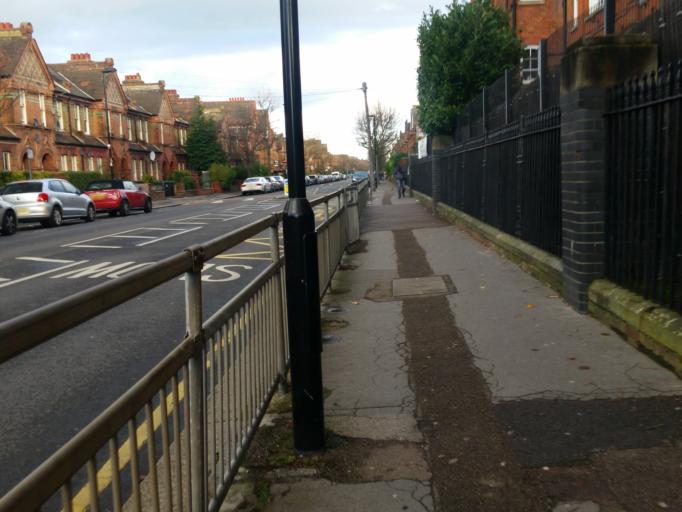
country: GB
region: England
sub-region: Greater London
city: Harringay
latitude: 51.5955
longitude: -0.1036
